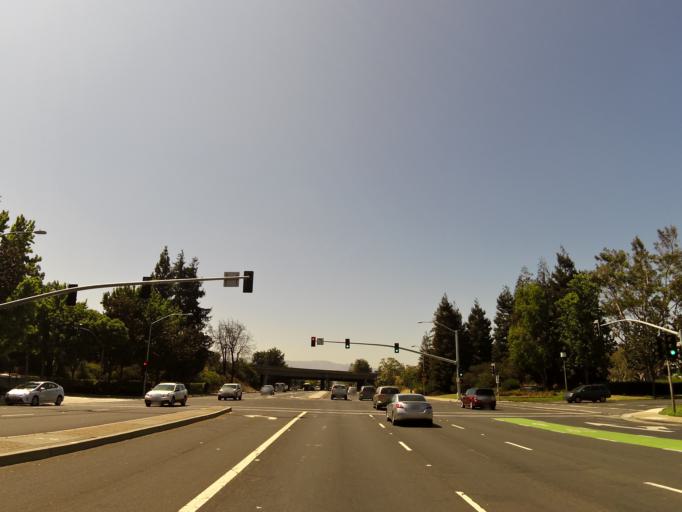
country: US
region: California
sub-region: Santa Clara County
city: Cupertino
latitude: 37.3231
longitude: -121.9972
